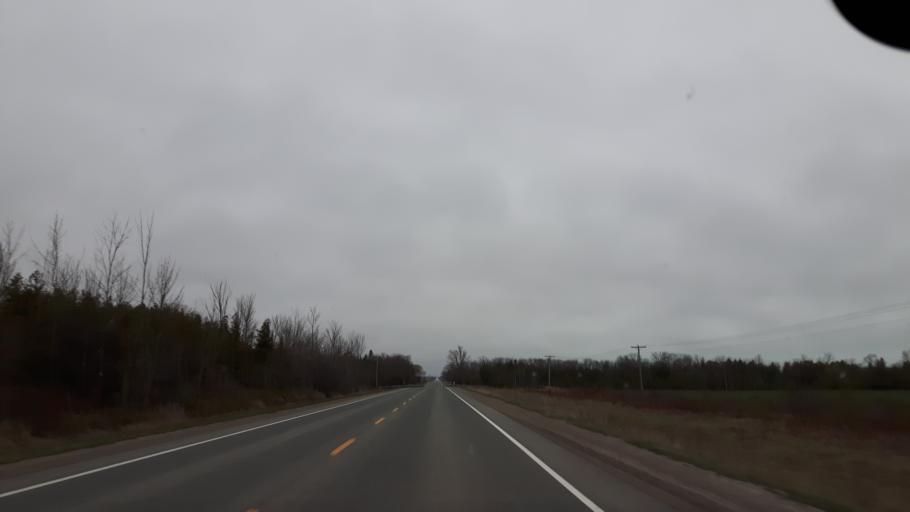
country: CA
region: Ontario
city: Goderich
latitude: 43.6571
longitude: -81.7057
